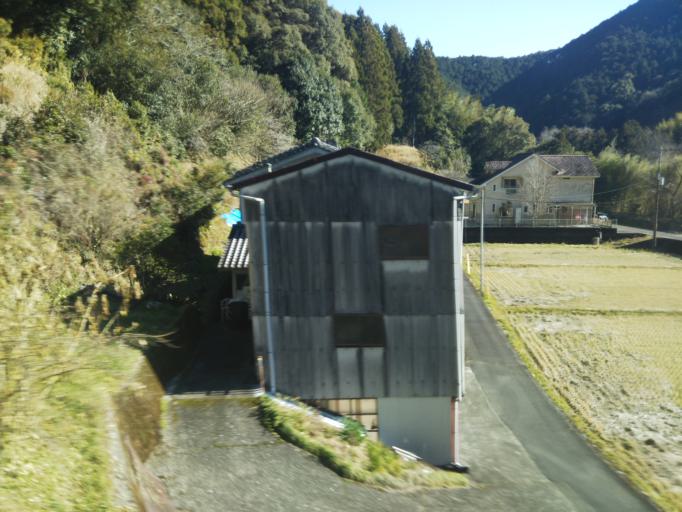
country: JP
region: Kochi
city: Nakamura
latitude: 33.1174
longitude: 133.1139
